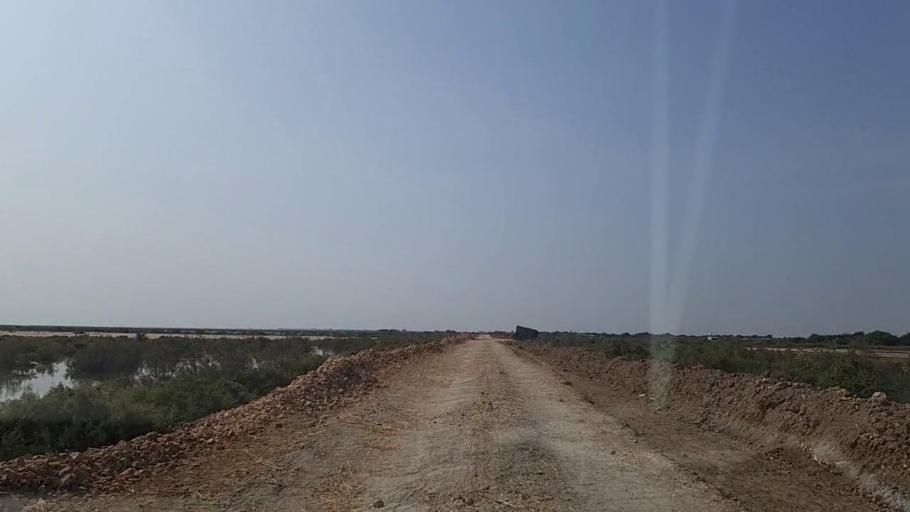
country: PK
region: Sindh
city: Chuhar Jamali
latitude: 24.1993
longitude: 67.8293
